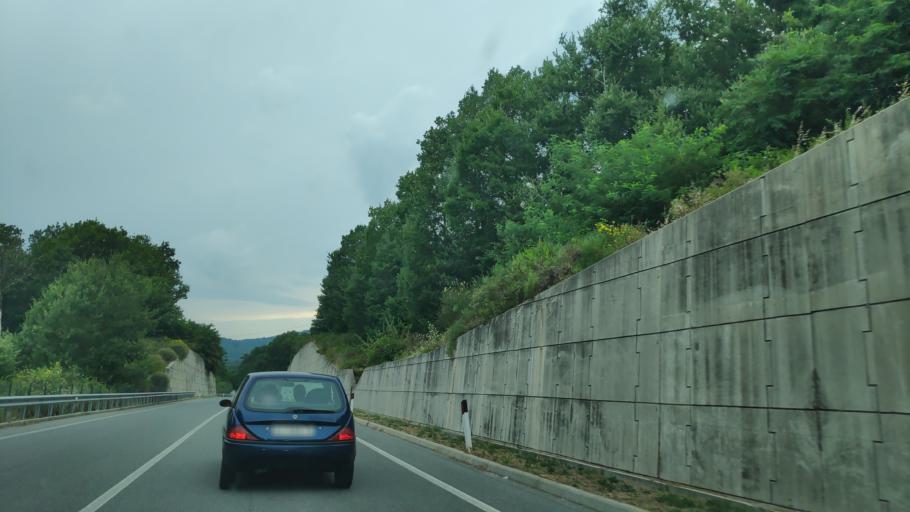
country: IT
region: Calabria
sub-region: Provincia di Catanzaro
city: Chiaravalle Centrale
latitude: 38.6672
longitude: 16.4004
